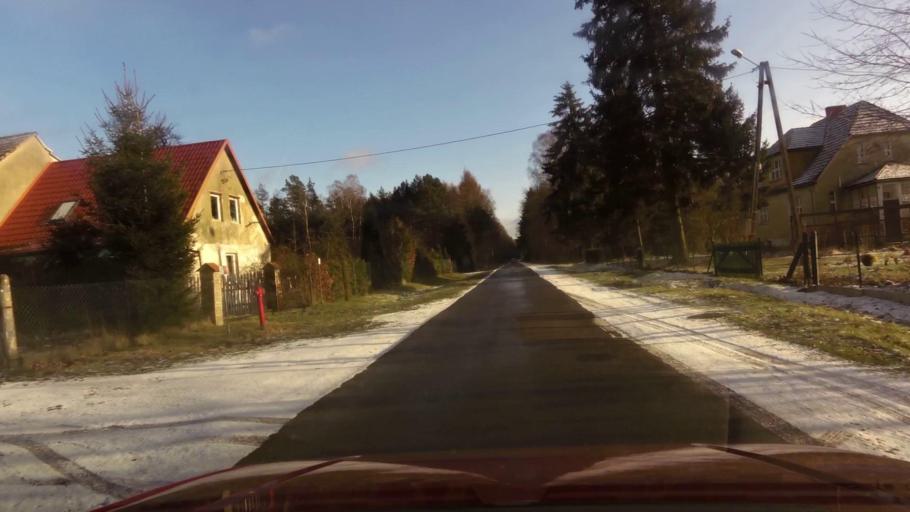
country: PL
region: West Pomeranian Voivodeship
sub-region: Powiat bialogardzki
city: Bialogard
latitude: 54.0903
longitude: 16.0699
